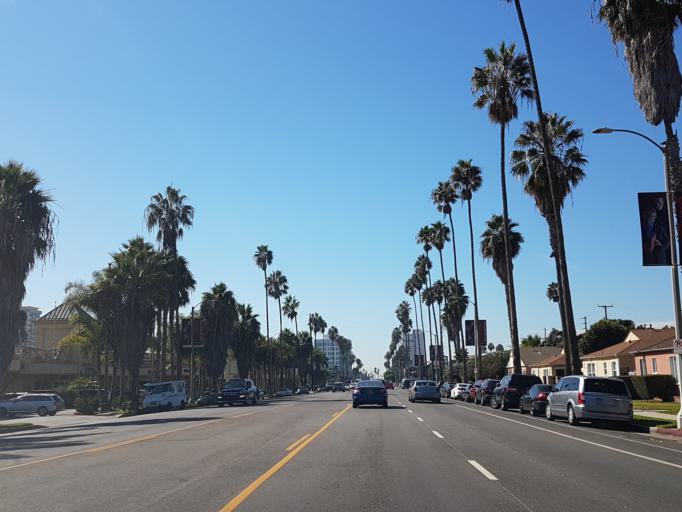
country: US
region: California
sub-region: Los Angeles County
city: Marina del Rey
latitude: 33.9840
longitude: -118.4589
